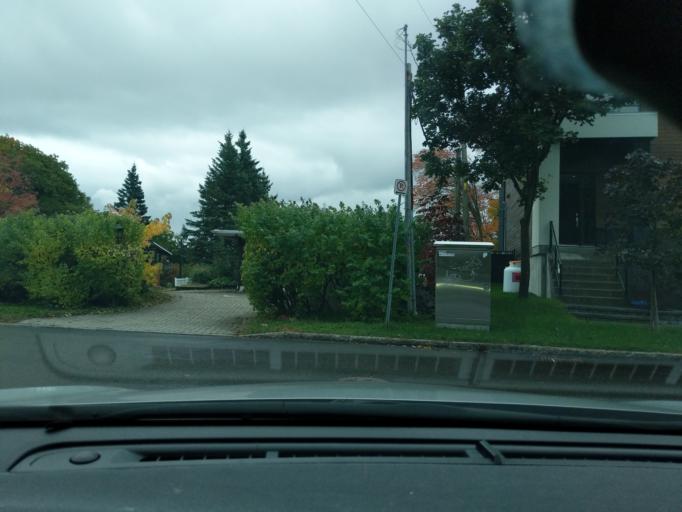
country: CA
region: Quebec
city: Quebec
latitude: 46.7641
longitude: -71.2688
